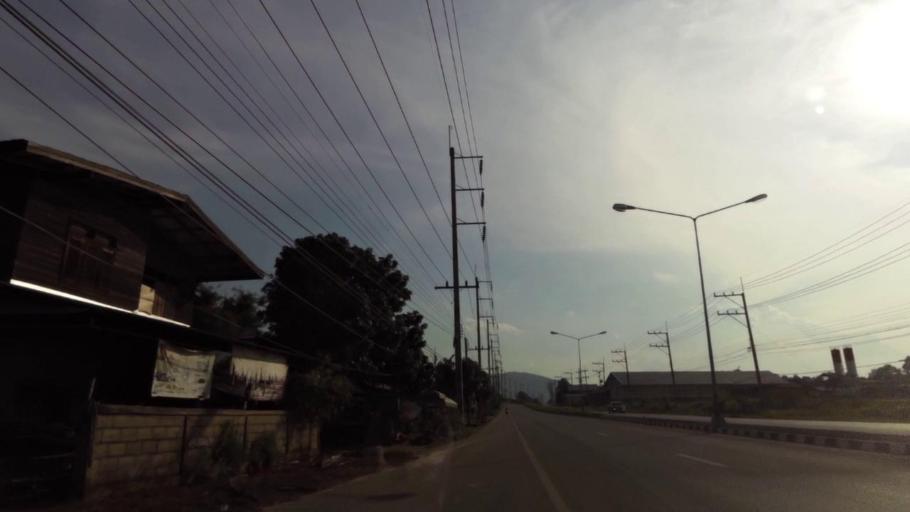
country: TH
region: Chiang Rai
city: Khun Tan
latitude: 19.9018
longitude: 100.2960
